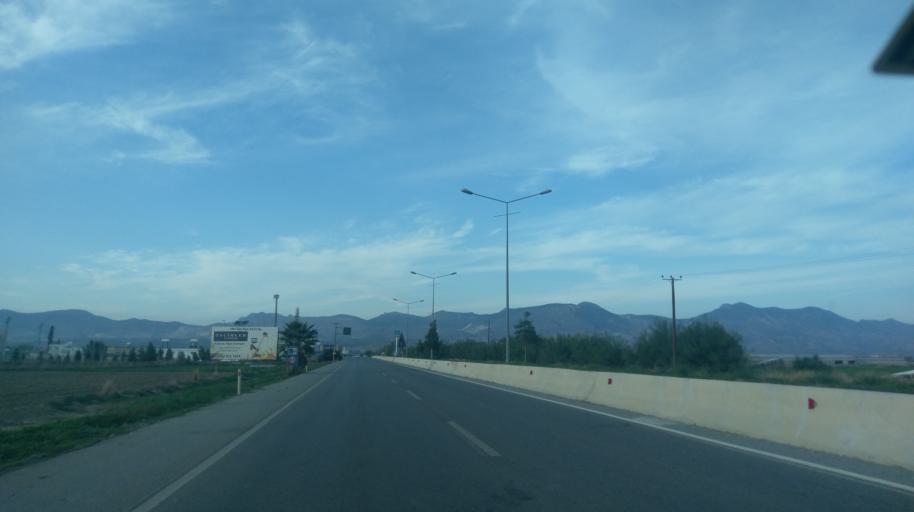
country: CY
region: Lefkosia
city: Geri
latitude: 35.2053
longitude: 33.4992
